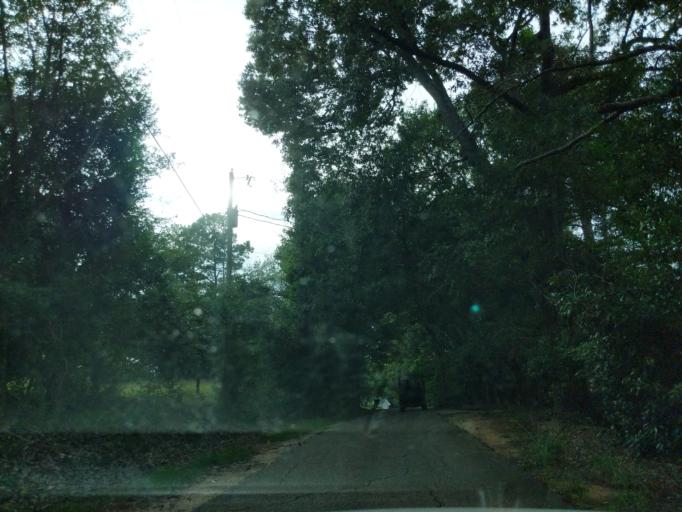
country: US
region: South Carolina
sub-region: Aiken County
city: North Augusta
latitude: 33.5322
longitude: -81.9919
